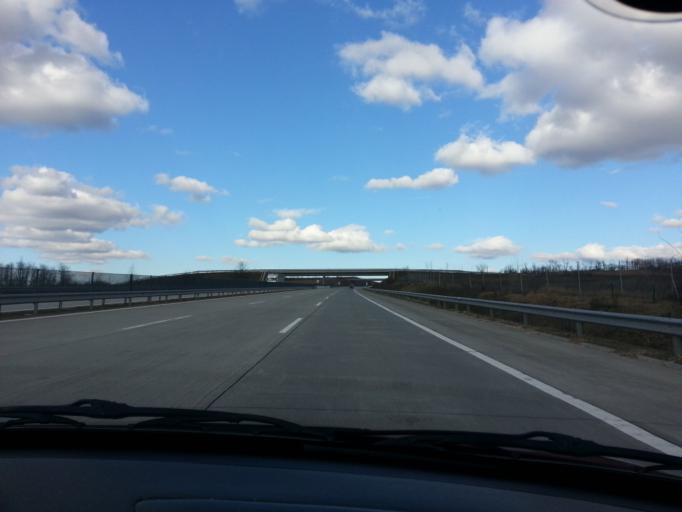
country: HU
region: Pest
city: Nagytarcsa
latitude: 47.5289
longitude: 19.3045
